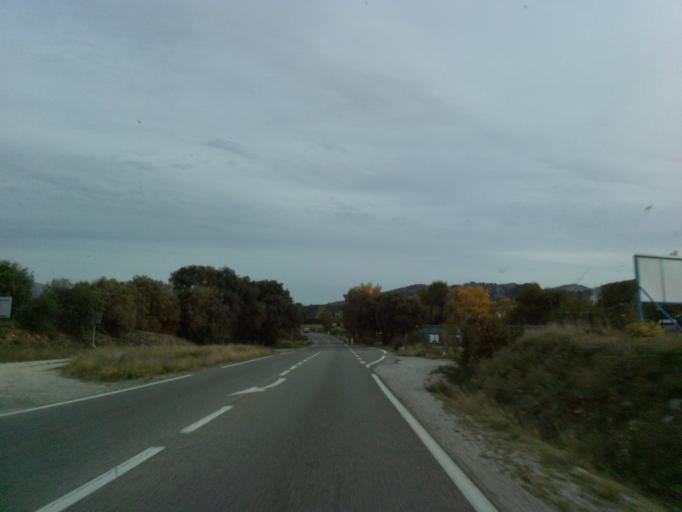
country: FR
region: Provence-Alpes-Cote d'Azur
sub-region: Departement des Alpes-de-Haute-Provence
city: Peipin
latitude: 44.1358
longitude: 5.9702
